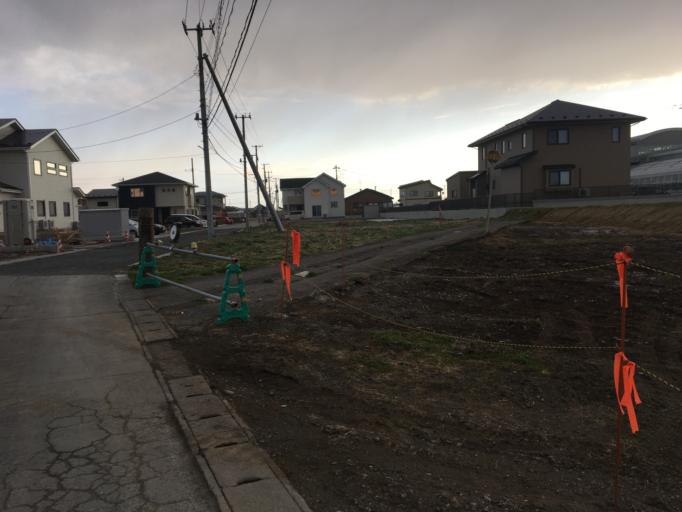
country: JP
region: Aomori
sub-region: Hachinohe Shi
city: Uchimaru
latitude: 40.5084
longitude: 141.4280
